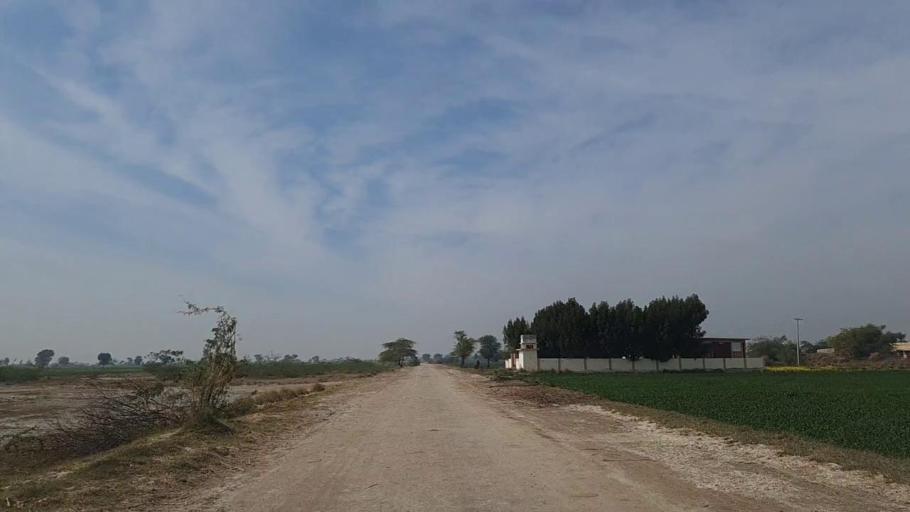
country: PK
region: Sindh
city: Nawabshah
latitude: 26.3276
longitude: 68.4357
